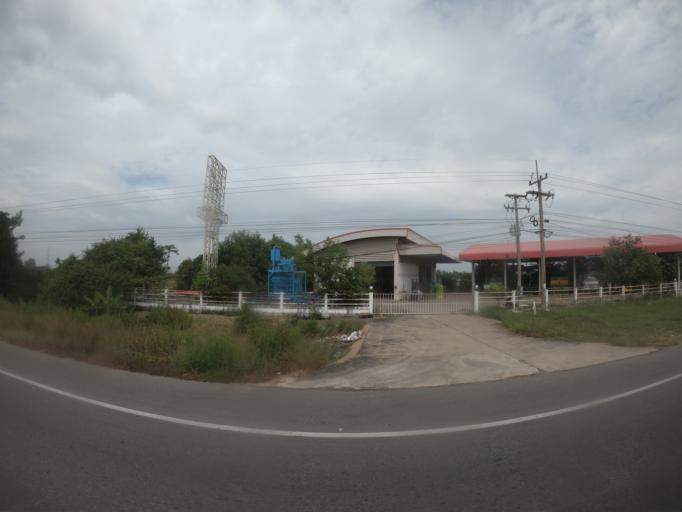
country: TH
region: Roi Et
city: Changhan
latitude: 16.0894
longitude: 103.5532
